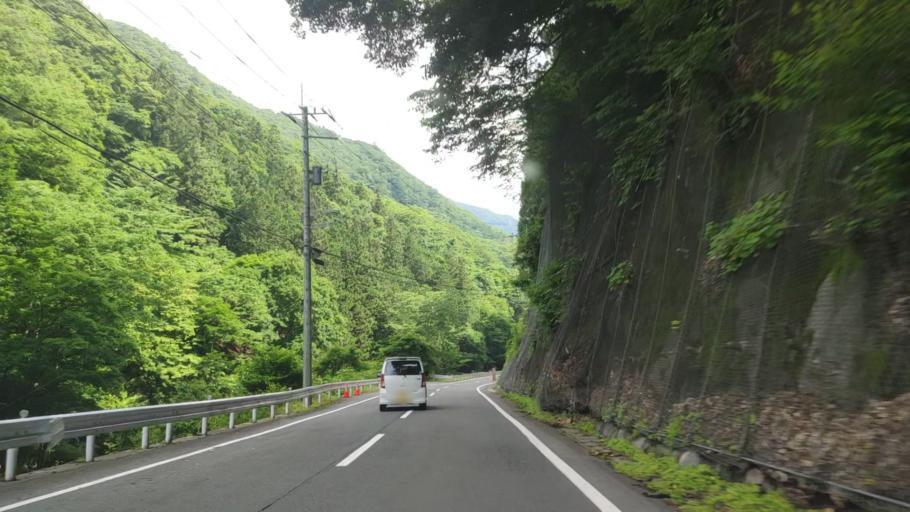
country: JP
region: Gunma
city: Tomioka
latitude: 36.0980
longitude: 138.7169
